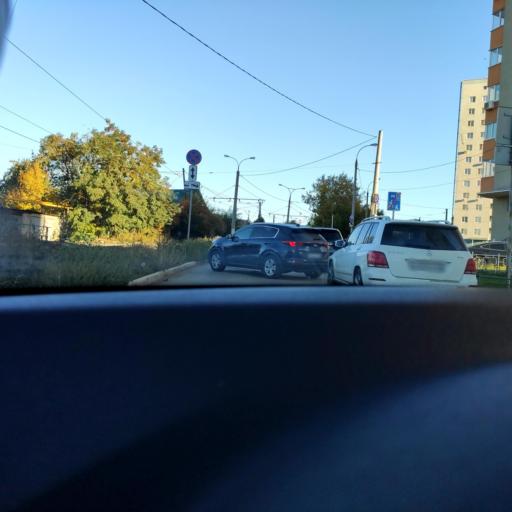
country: RU
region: Samara
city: Samara
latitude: 53.2189
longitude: 50.1706
